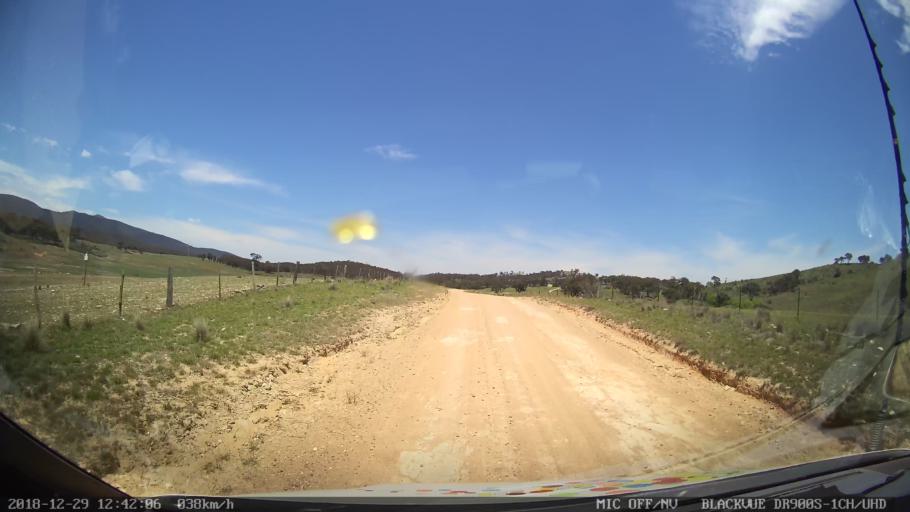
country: AU
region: Australian Capital Territory
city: Macarthur
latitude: -35.6105
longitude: 149.2206
